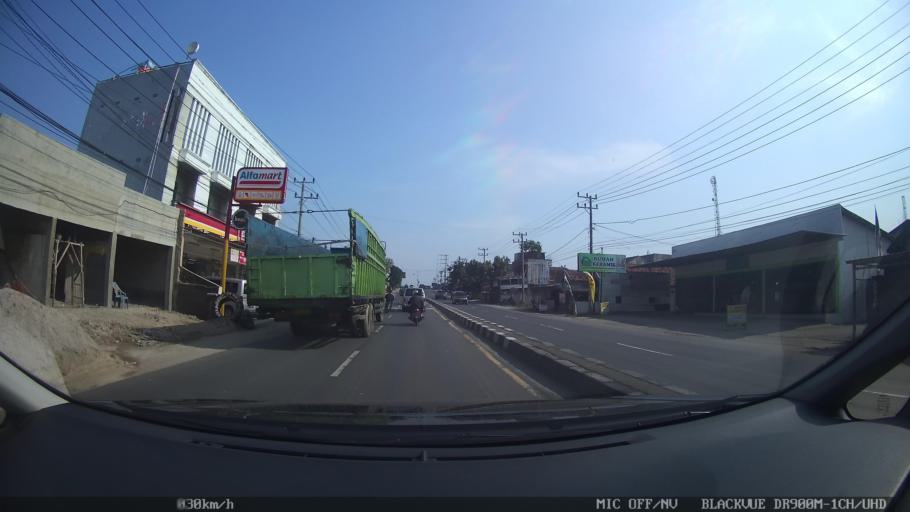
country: ID
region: Lampung
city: Natar
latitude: -5.2951
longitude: 105.1920
